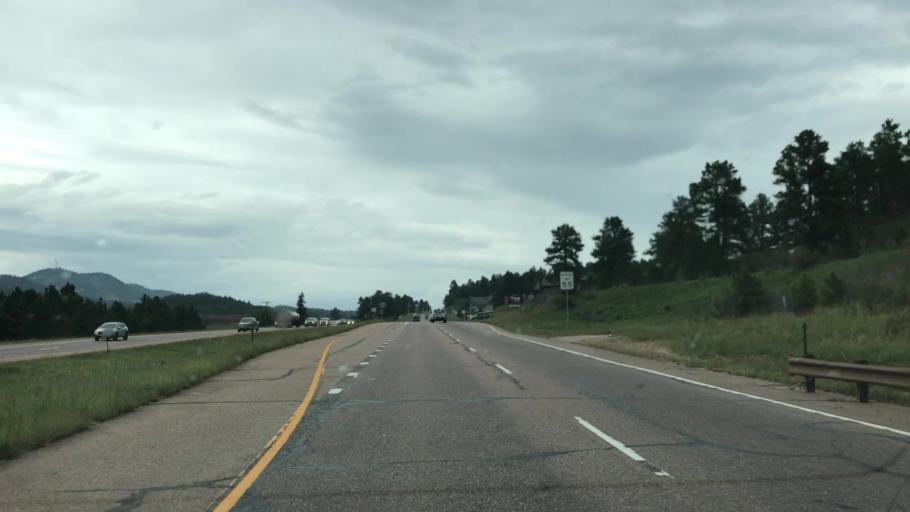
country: US
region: Colorado
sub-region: El Paso County
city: Cascade-Chipita Park
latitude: 38.9654
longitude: -105.0321
